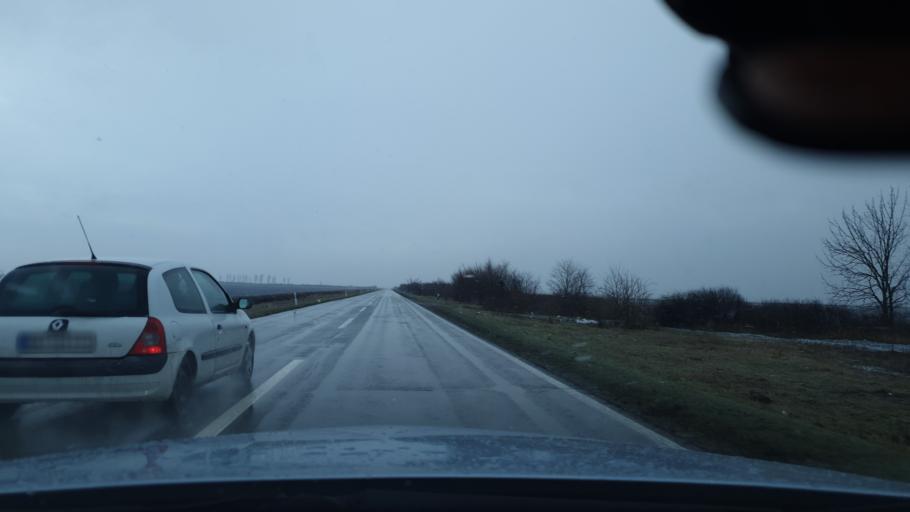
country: RS
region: Autonomna Pokrajina Vojvodina
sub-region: Juznobanatski Okrug
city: Pancevo
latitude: 44.8541
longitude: 20.7612
